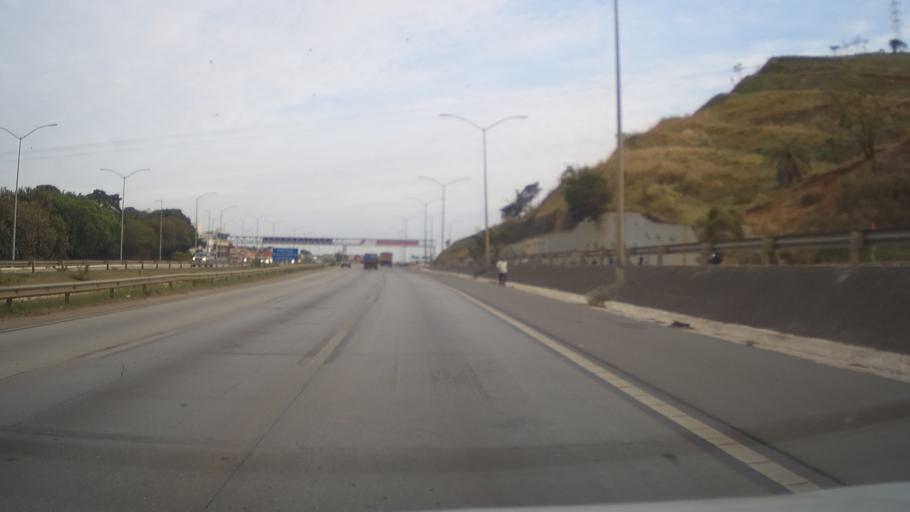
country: BR
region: Minas Gerais
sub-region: Vespasiano
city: Vespasiano
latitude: -19.7793
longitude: -43.9485
